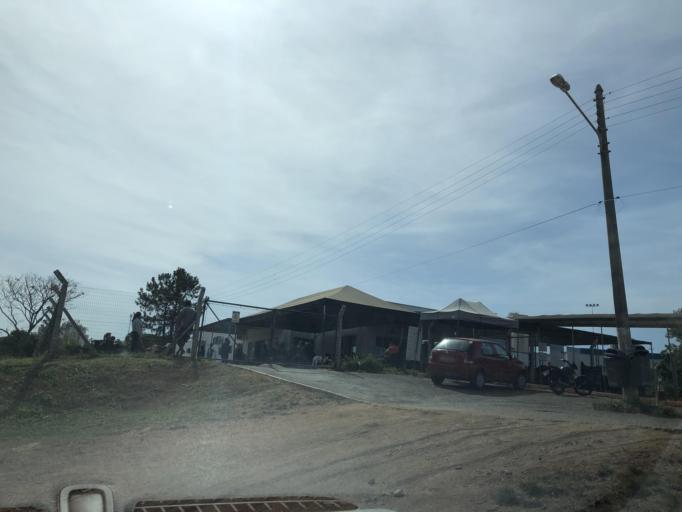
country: BR
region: Federal District
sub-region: Brasilia
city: Brasilia
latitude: -15.8165
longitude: -48.0729
